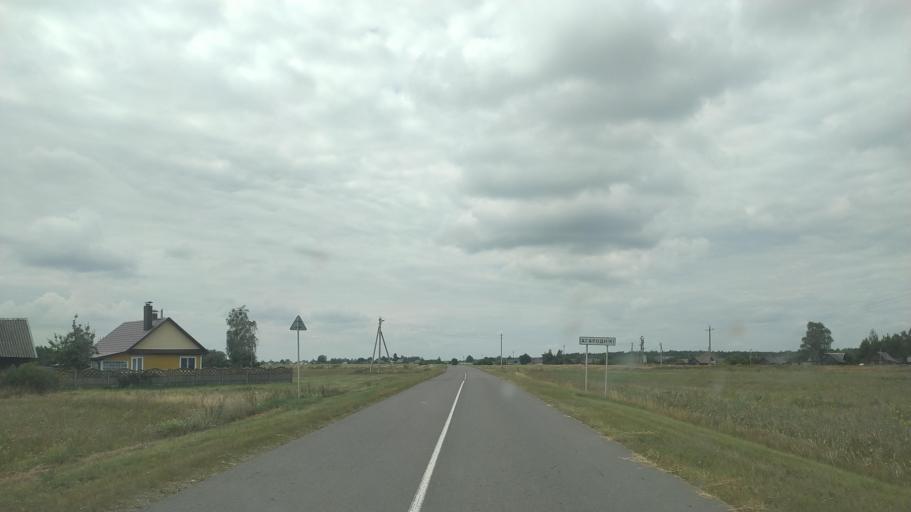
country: BY
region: Brest
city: Byelaazyorsk
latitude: 52.5397
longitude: 25.1204
